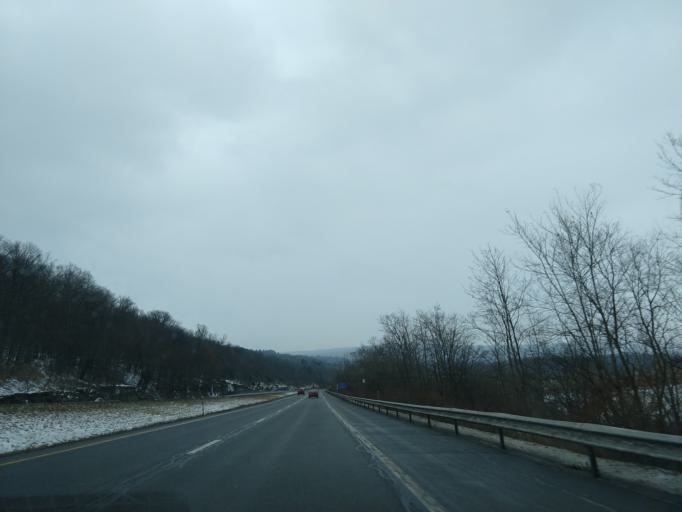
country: US
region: New York
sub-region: Tompkins County
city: Cayuga Heights
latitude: 42.4691
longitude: -76.4999
